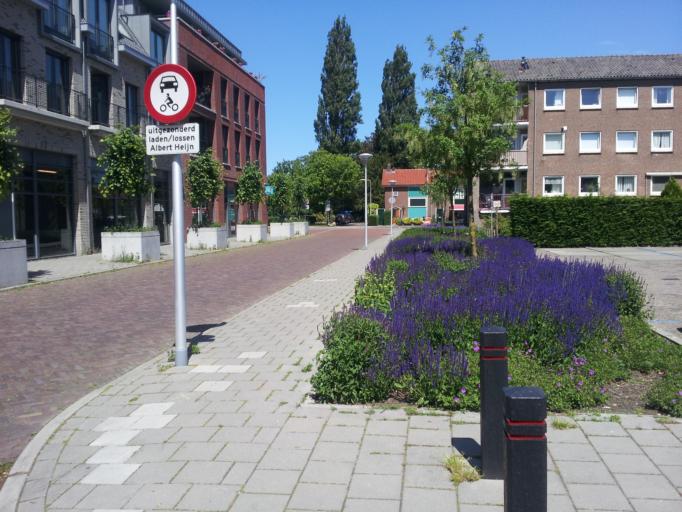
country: NL
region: South Holland
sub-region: Gemeente Voorschoten
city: Voorschoten
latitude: 52.1263
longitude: 4.4489
